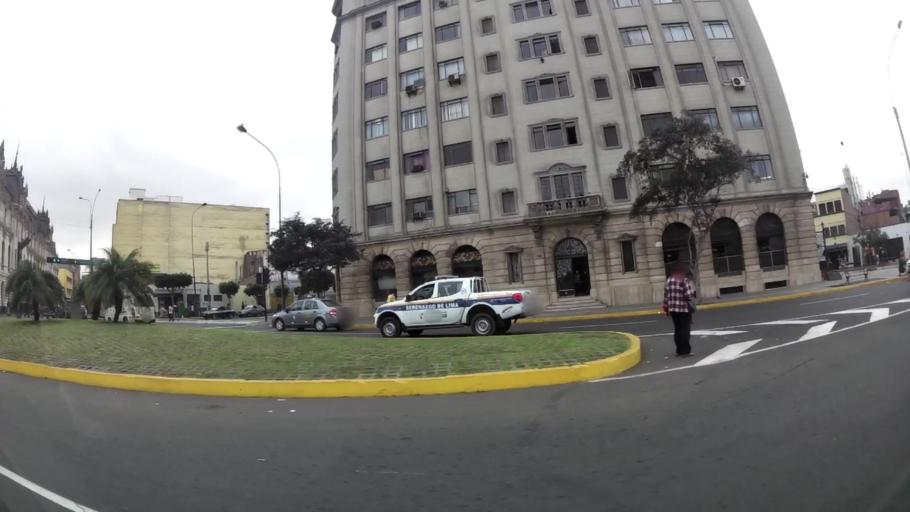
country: PE
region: Lima
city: Lima
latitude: -12.0559
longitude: -77.0359
